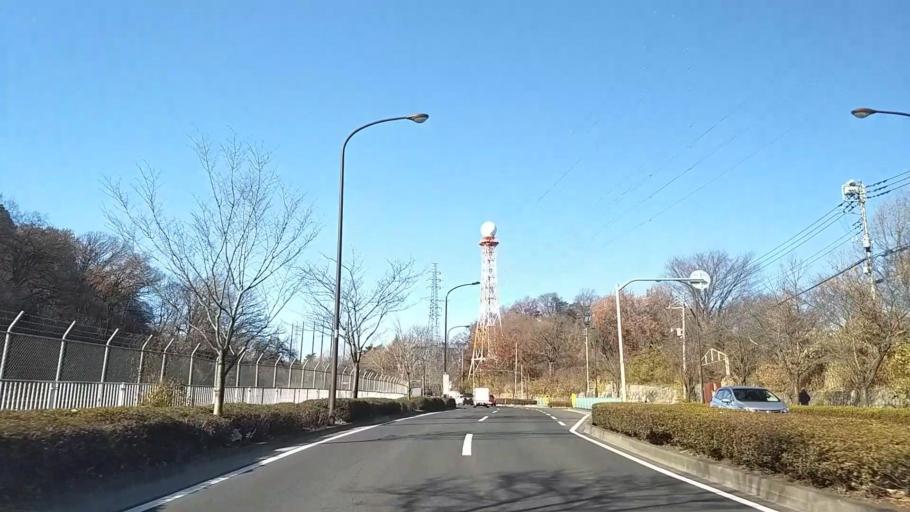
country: JP
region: Tokyo
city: Kokubunji
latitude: 35.6461
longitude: 139.4772
